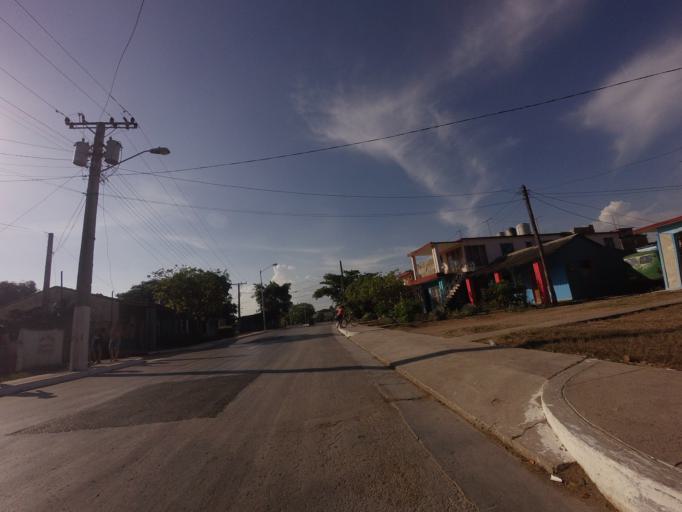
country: CU
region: Ciego de Avila
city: Ciego de Avila
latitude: 21.8438
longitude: -78.7718
